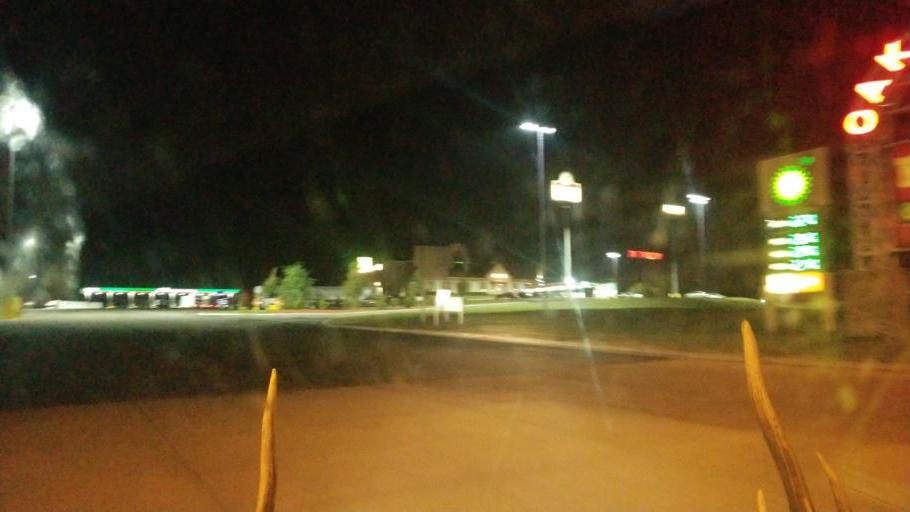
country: US
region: Missouri
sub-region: Jackson County
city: Oak Grove
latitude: 39.0142
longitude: -94.1290
